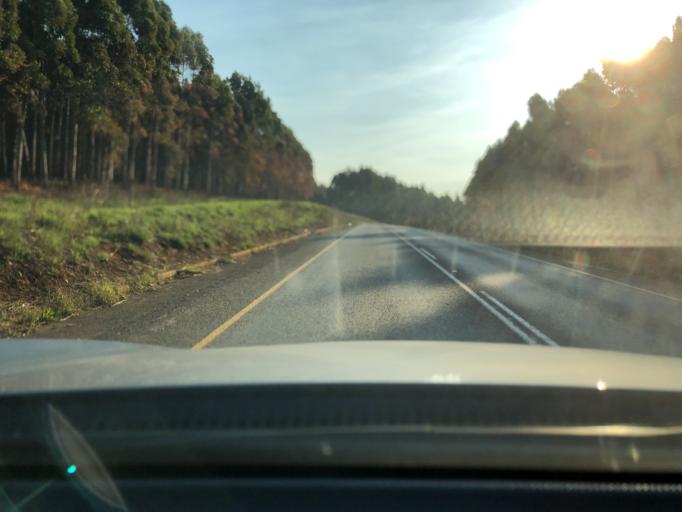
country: ZA
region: KwaZulu-Natal
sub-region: Sisonke District Municipality
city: Ixopo
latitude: -30.2255
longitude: 30.1269
